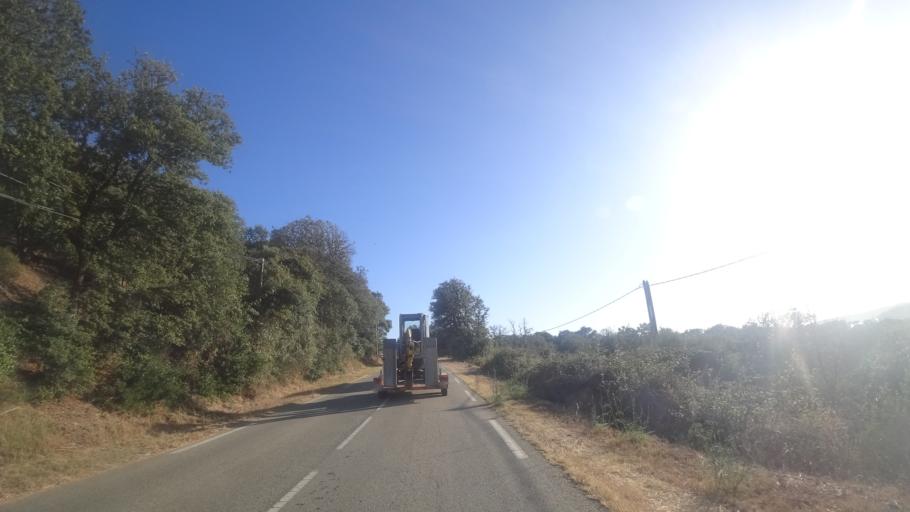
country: FR
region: Corsica
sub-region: Departement de la Corse-du-Sud
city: Cargese
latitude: 42.1487
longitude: 8.6042
